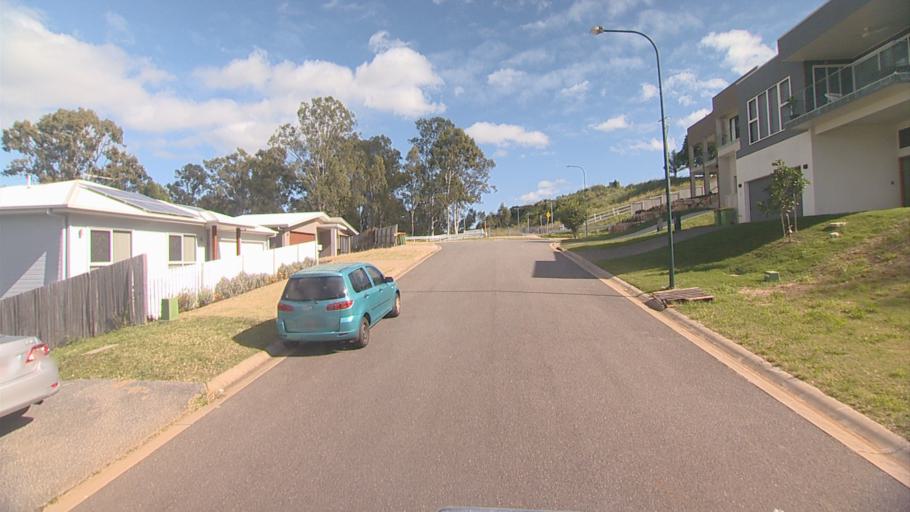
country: AU
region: Queensland
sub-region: Logan
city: Woodridge
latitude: -27.6145
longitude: 153.1025
